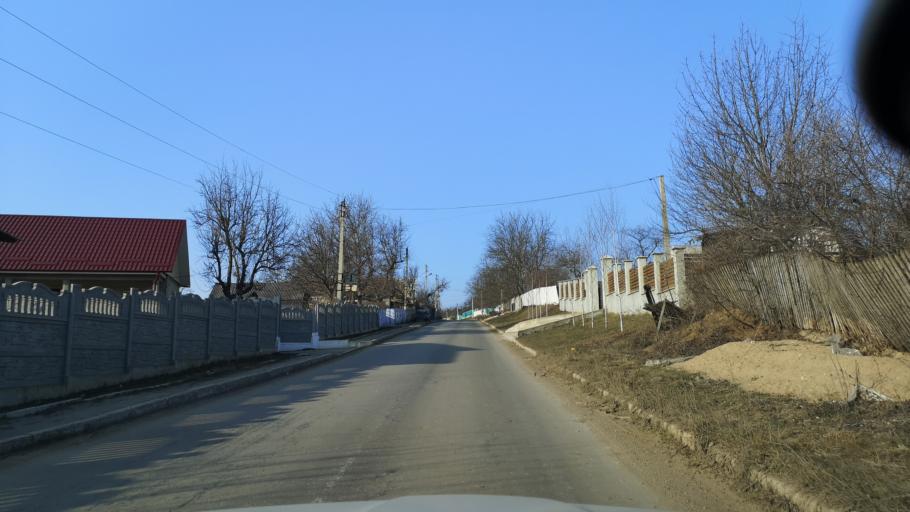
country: MD
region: Stinga Nistrului
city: Bucovat
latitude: 47.1114
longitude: 28.5099
